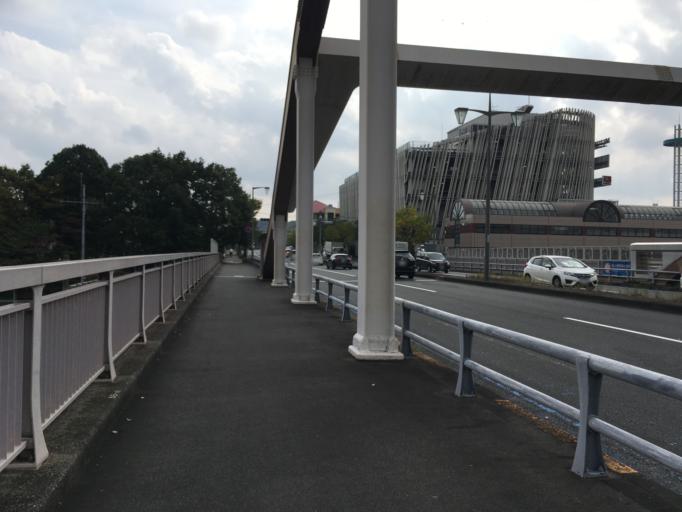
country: JP
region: Tokyo
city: Hino
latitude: 35.6151
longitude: 139.3810
